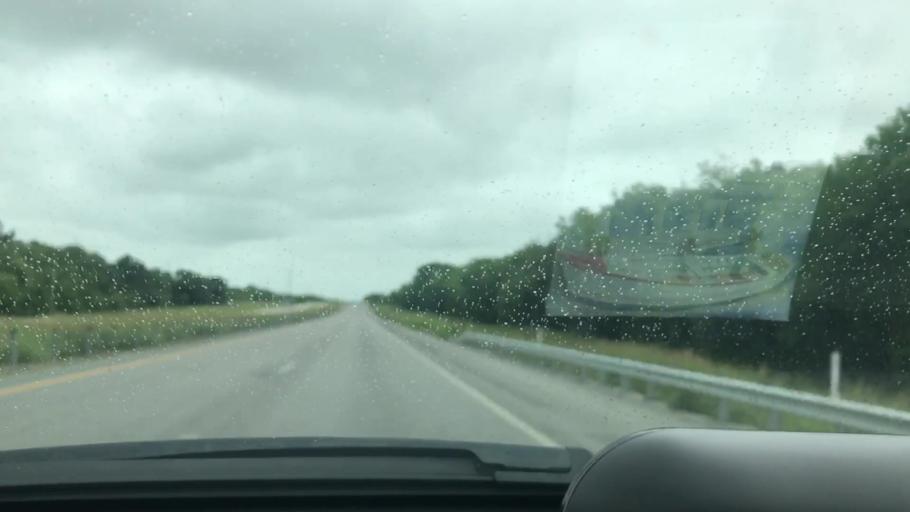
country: US
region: Oklahoma
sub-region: Coal County
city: Coalgate
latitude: 34.6185
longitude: -95.9662
